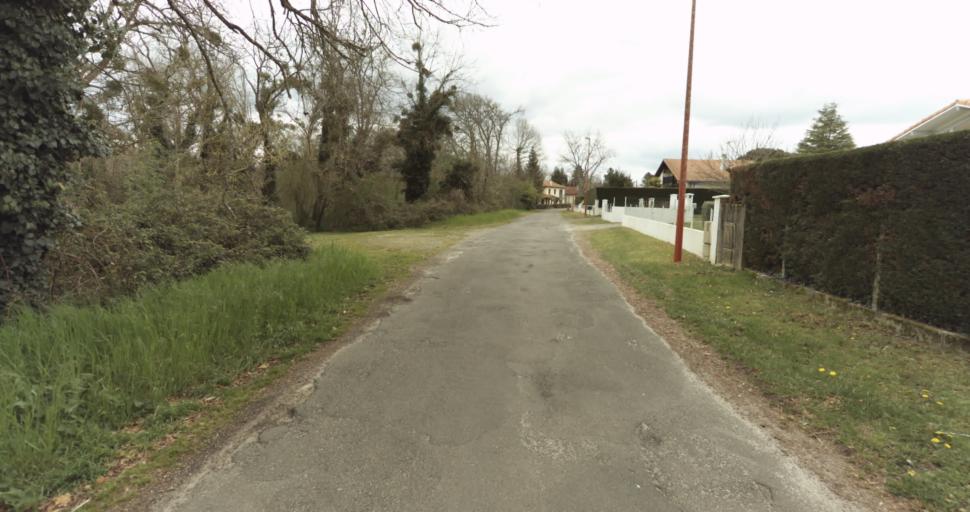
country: FR
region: Aquitaine
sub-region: Departement des Landes
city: Roquefort
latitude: 44.0383
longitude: -0.3150
